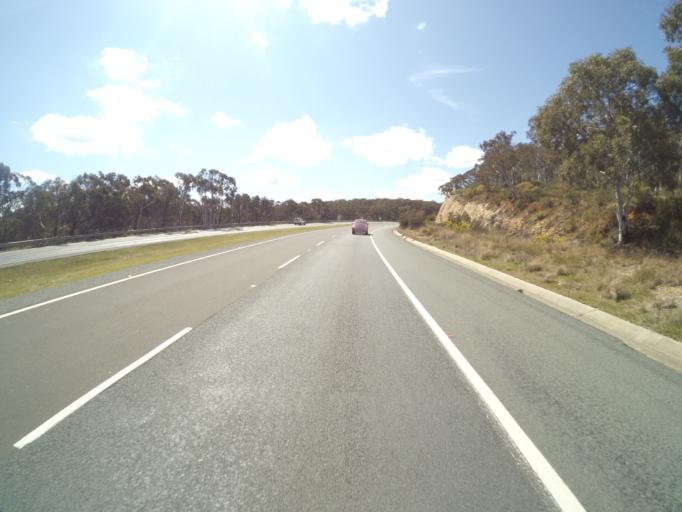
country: AU
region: New South Wales
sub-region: Goulburn Mulwaree
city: Goulburn
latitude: -34.7435
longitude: 149.7579
